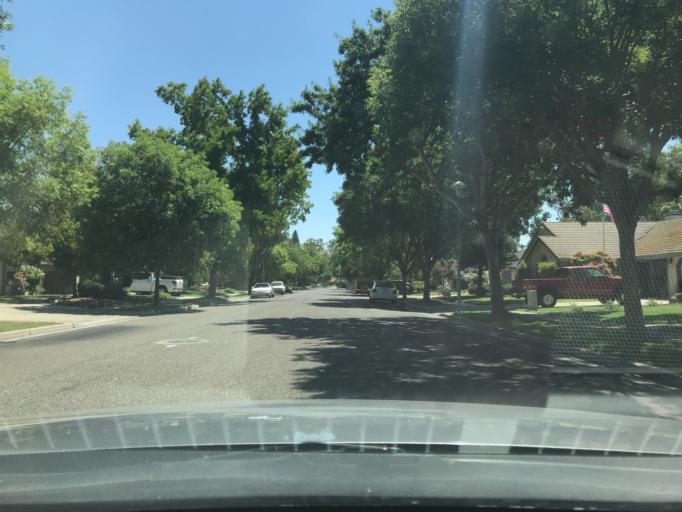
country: US
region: California
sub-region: Merced County
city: Merced
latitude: 37.3252
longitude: -120.4926
